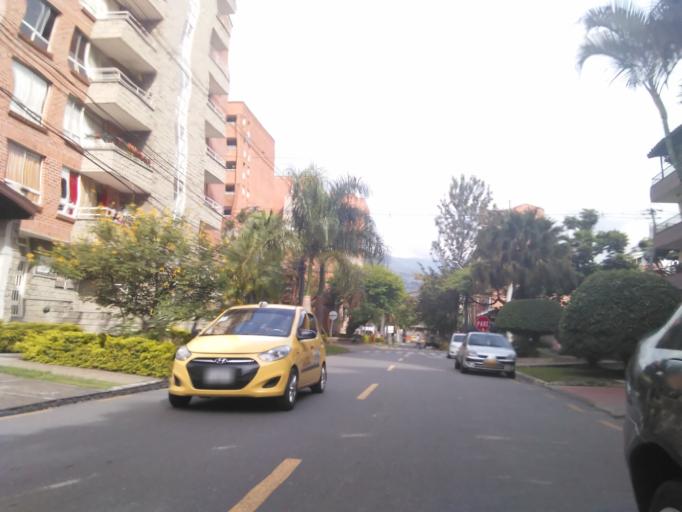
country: CO
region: Antioquia
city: Medellin
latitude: 6.2401
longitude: -75.5803
